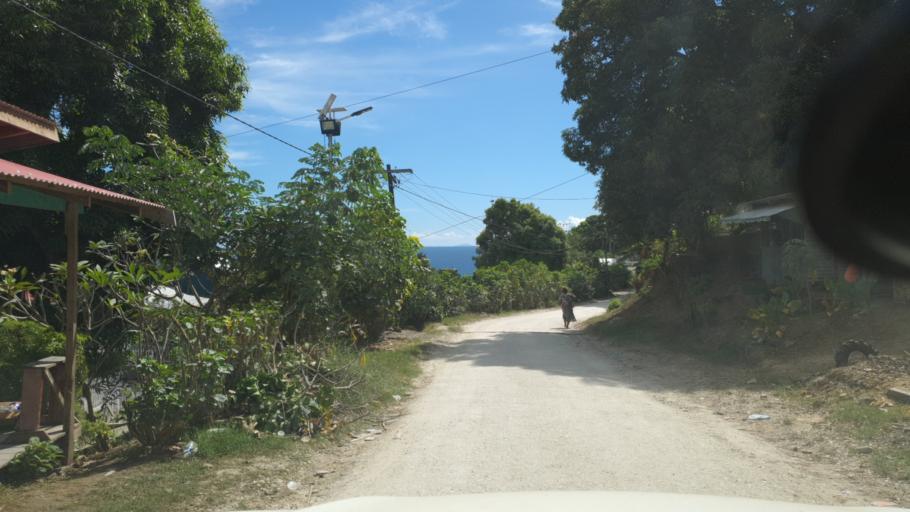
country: SB
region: Guadalcanal
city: Honiara
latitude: -9.4370
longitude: 159.9803
